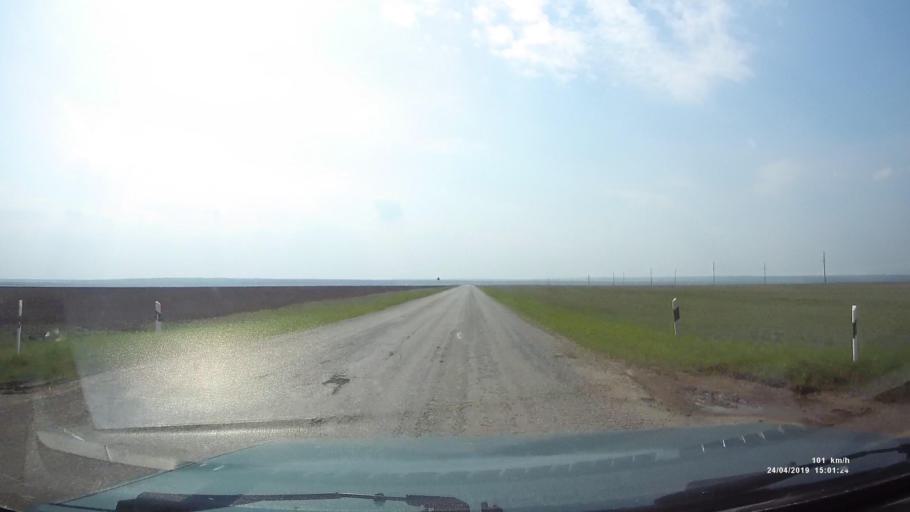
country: RU
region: Rostov
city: Remontnoye
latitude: 46.5660
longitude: 43.5343
